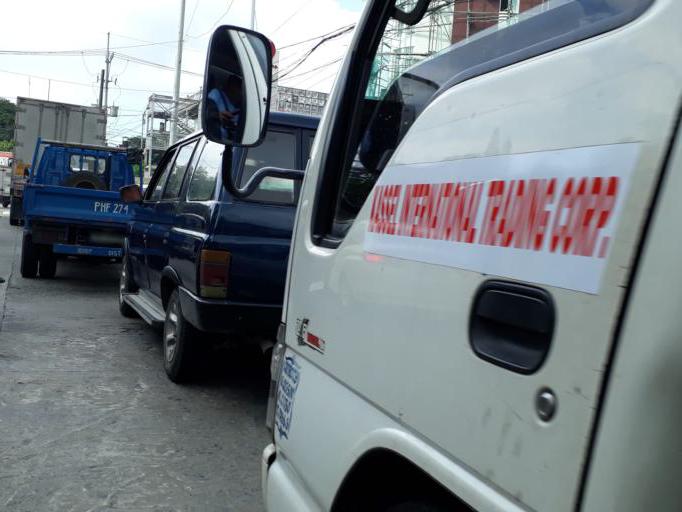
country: PH
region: Metro Manila
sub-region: City of Manila
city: Manila
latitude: 14.6252
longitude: 120.9891
